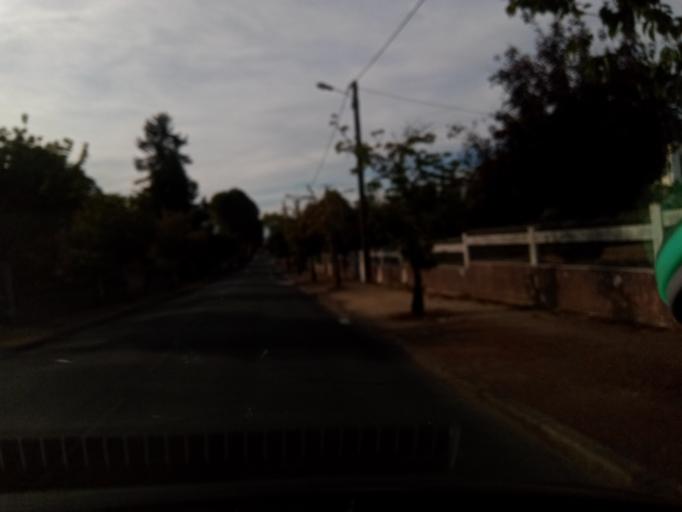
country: FR
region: Poitou-Charentes
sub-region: Departement de la Vienne
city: Montmorillon
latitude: 46.4191
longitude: 0.8779
